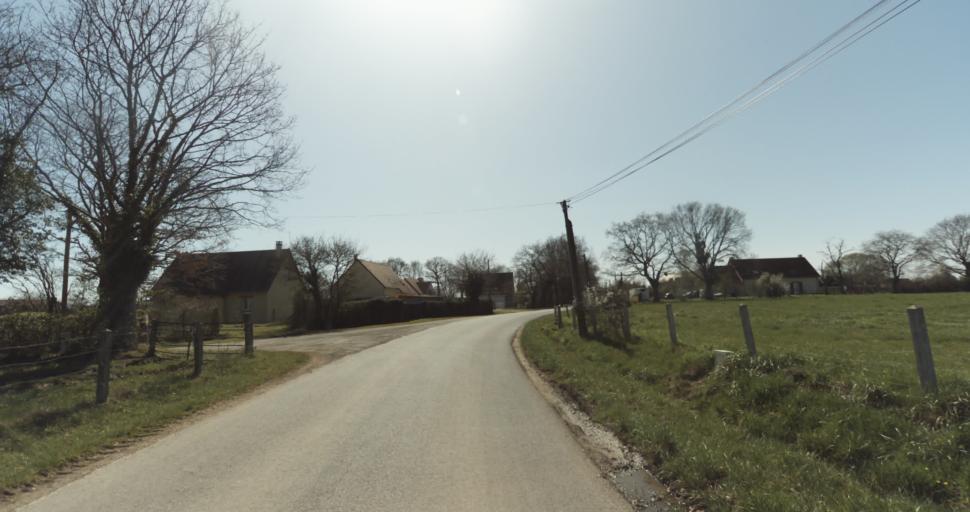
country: FR
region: Lower Normandy
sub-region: Departement du Calvados
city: Saint-Pierre-sur-Dives
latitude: 49.0095
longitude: -0.0068
